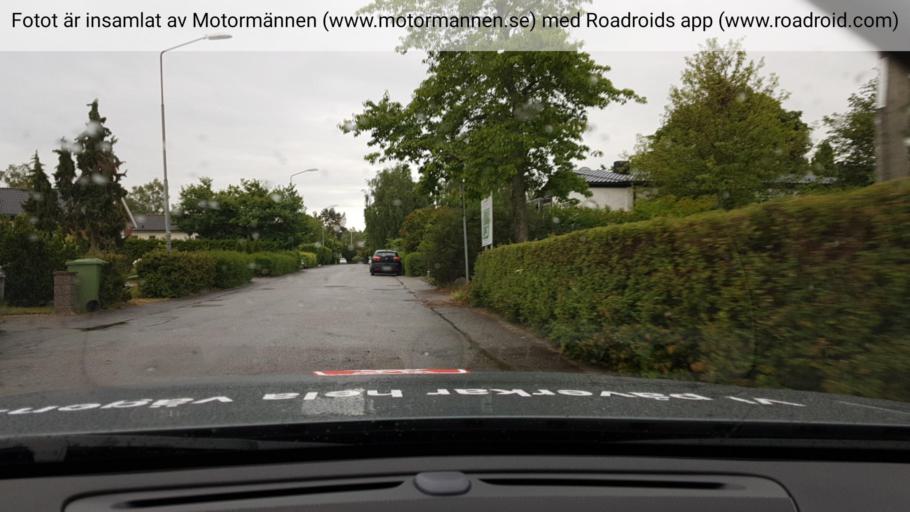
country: SE
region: Stockholm
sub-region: Vallentuna Kommun
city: Vallentuna
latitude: 59.5179
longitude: 18.0646
